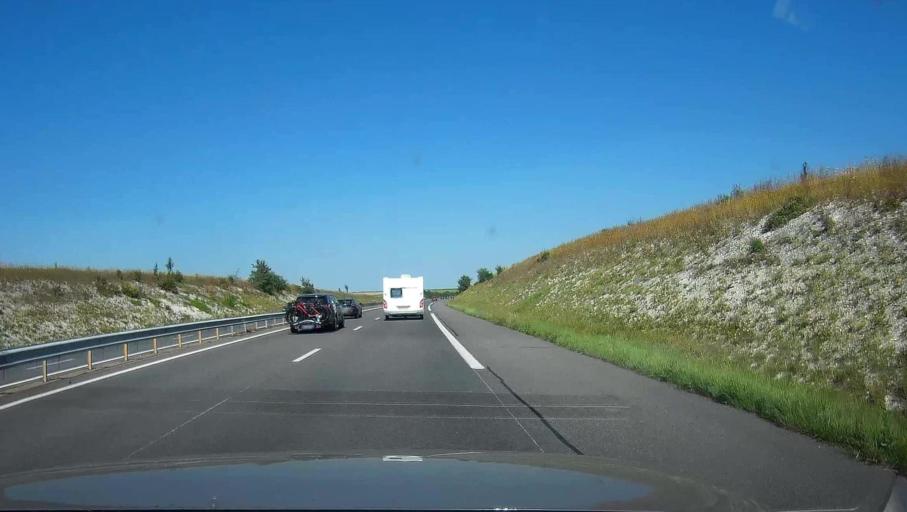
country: FR
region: Champagne-Ardenne
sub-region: Departement de l'Aube
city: Mailly-le-Camp
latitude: 48.6652
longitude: 4.1706
